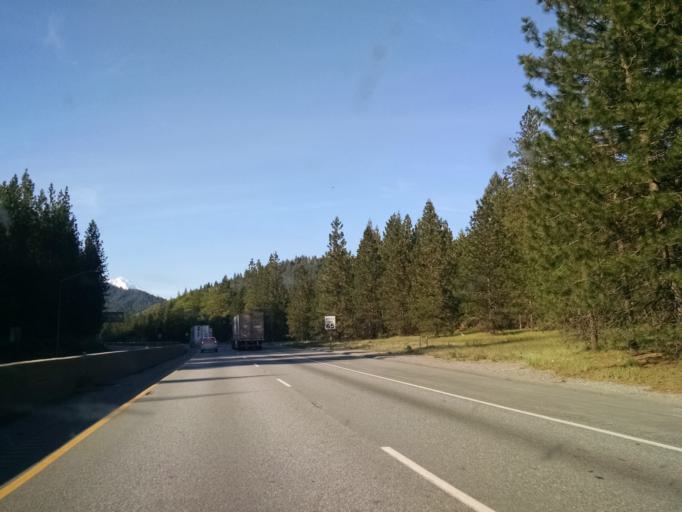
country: US
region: California
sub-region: Siskiyou County
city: Dunsmuir
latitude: 41.0730
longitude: -122.3573
